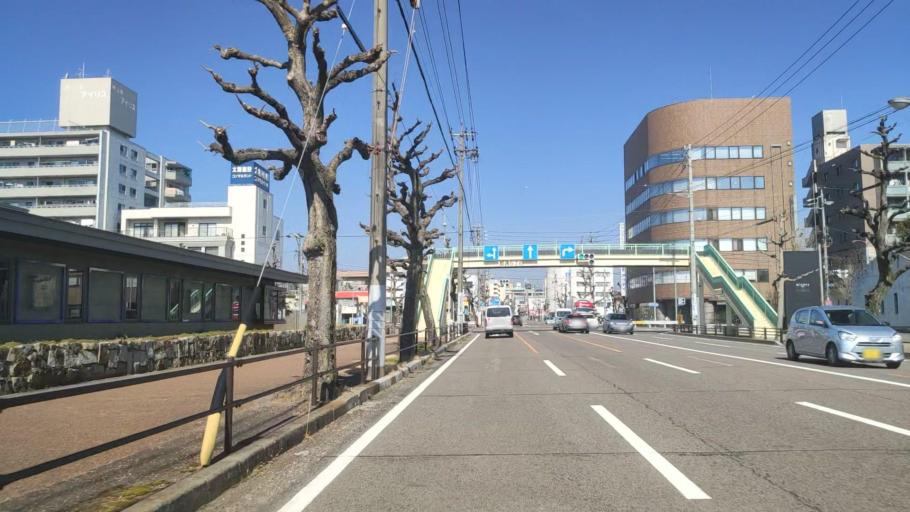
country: JP
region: Gifu
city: Gifu-shi
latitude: 35.4144
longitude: 136.7471
